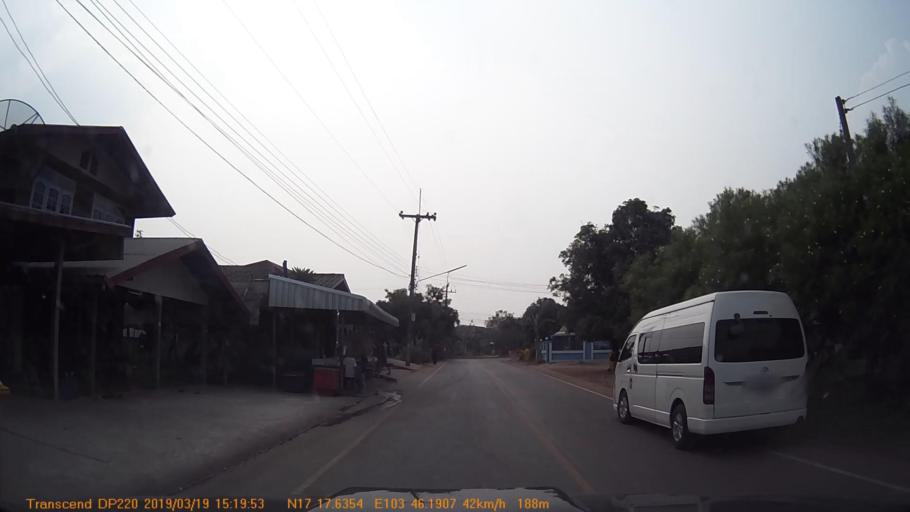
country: TH
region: Sakon Nakhon
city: Phanna Nikhom
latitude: 17.2940
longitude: 103.7697
